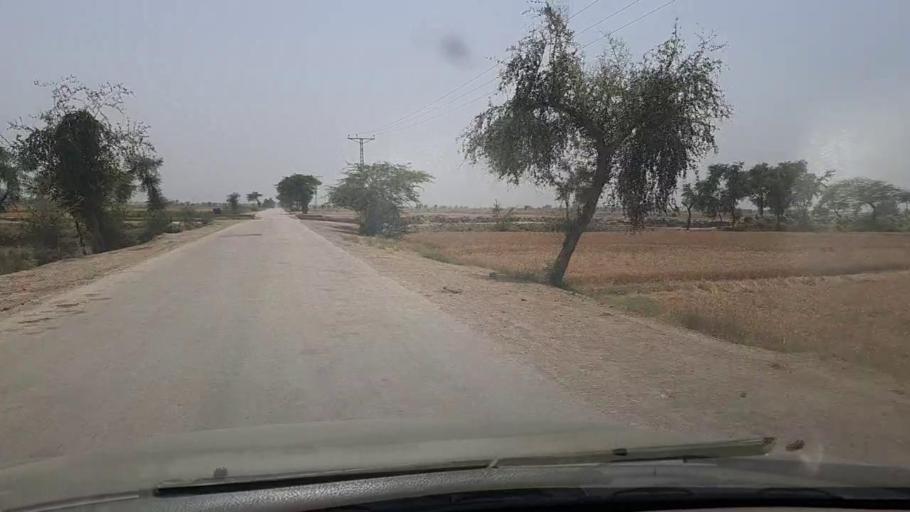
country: PK
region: Sindh
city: Miro Khan
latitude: 27.7092
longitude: 68.0642
